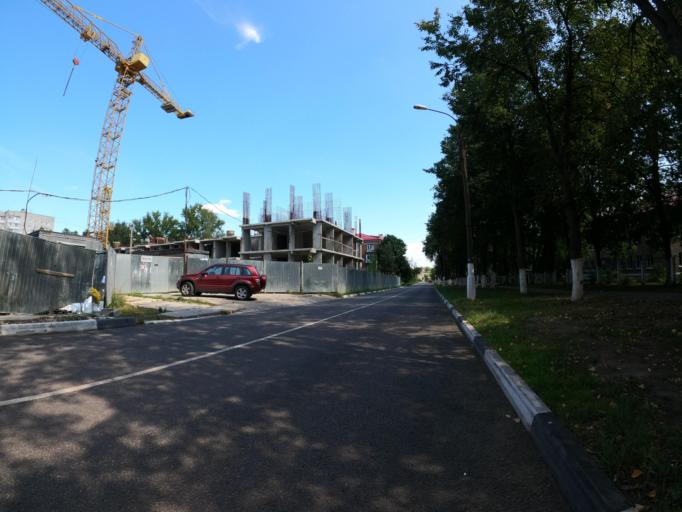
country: RU
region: Moskovskaya
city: Stupino
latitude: 54.8893
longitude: 38.0900
